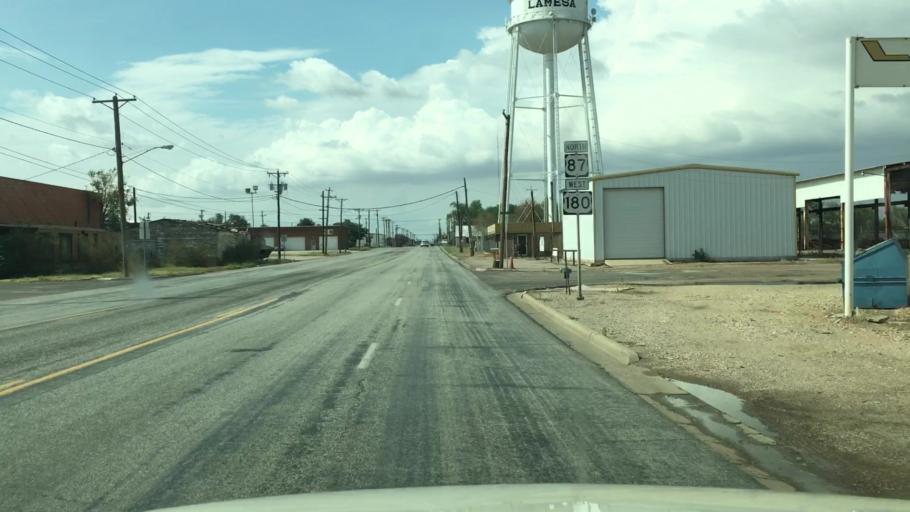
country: US
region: Texas
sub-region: Dawson County
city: Lamesa
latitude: 32.7294
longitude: -101.9479
